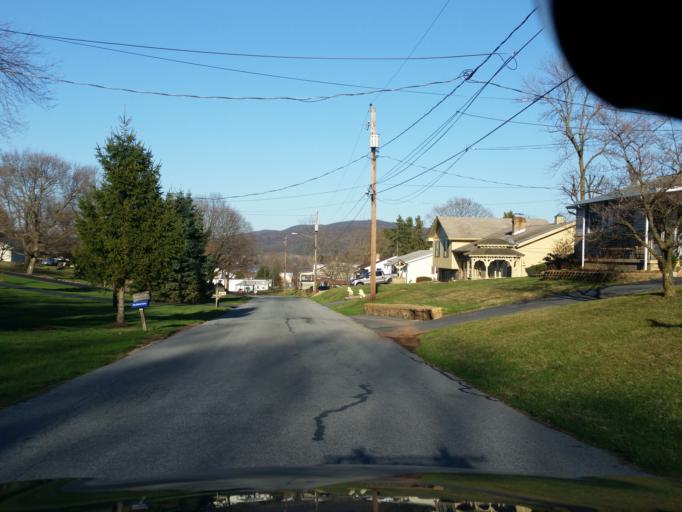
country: US
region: Pennsylvania
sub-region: Perry County
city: Marysville
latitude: 40.3404
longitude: -76.9359
